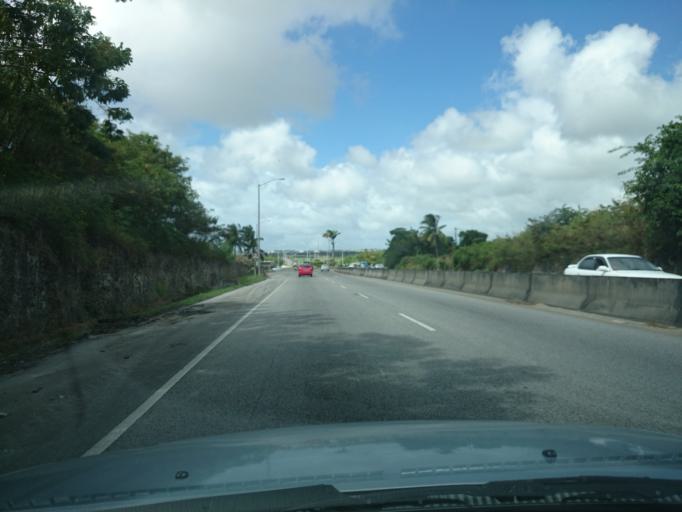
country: BB
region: Saint Michael
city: Bridgetown
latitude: 13.1122
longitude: -59.5823
